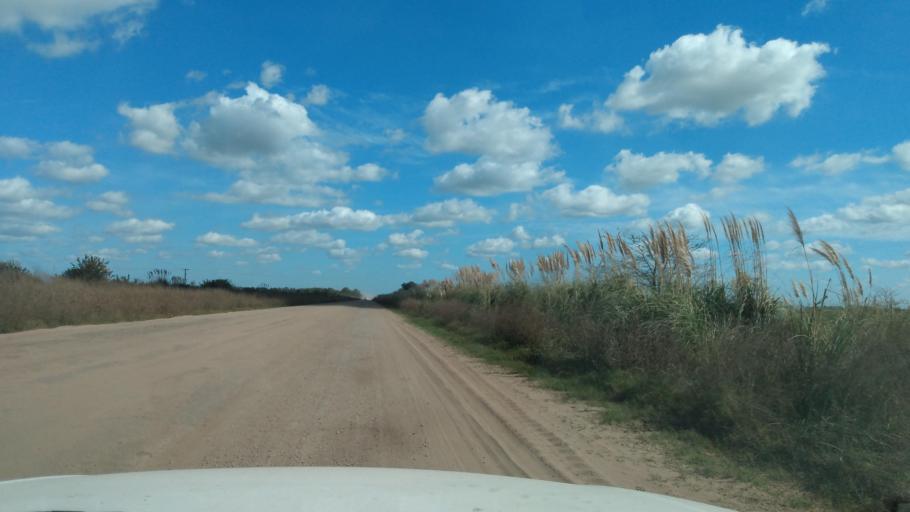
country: AR
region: Buenos Aires
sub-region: Partido de Navarro
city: Navarro
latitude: -35.0043
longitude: -59.3703
